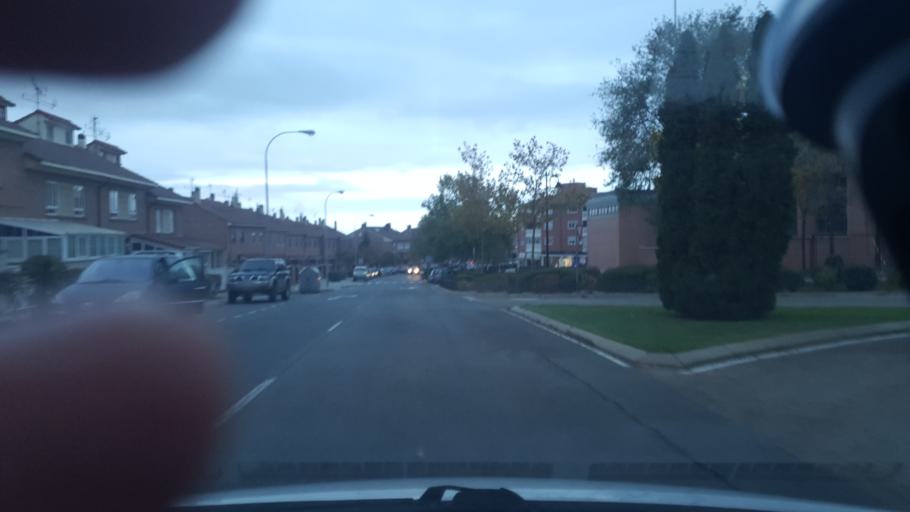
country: ES
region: Castille and Leon
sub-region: Provincia de Segovia
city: Segovia
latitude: 40.9286
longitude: -4.0983
